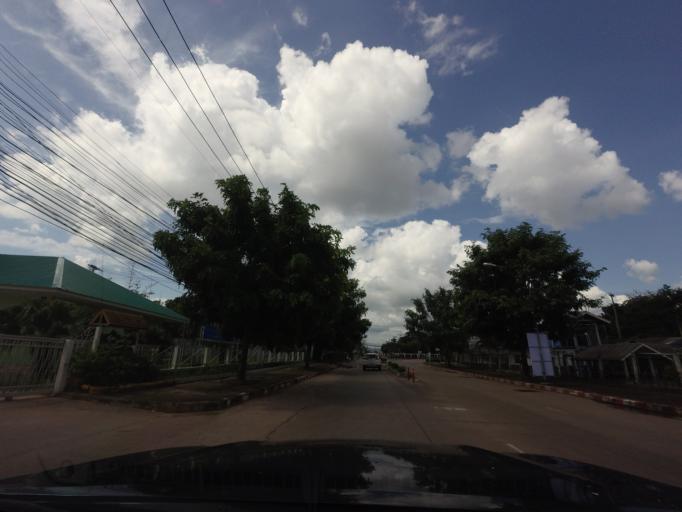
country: TH
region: Changwat Udon Thani
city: Udon Thani
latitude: 17.4227
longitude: 102.7768
